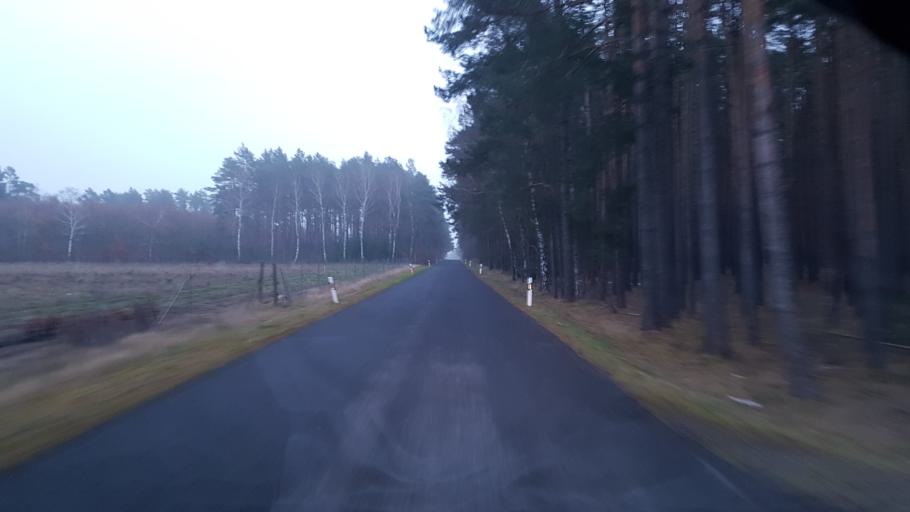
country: DE
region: Brandenburg
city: Bronkow
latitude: 51.6887
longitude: 13.9296
